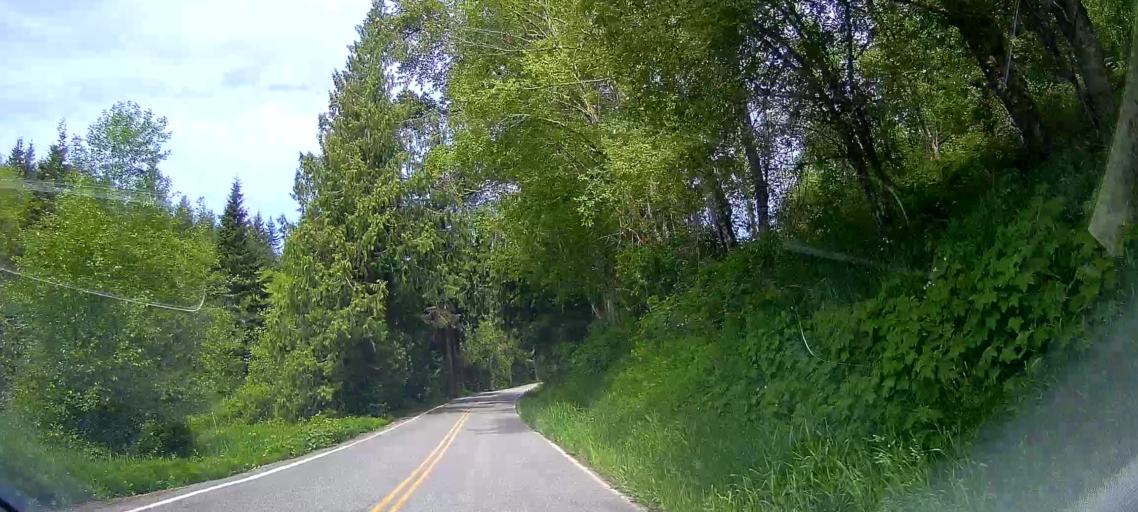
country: US
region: Washington
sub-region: Snohomish County
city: Bryant
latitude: 48.3216
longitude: -122.1602
